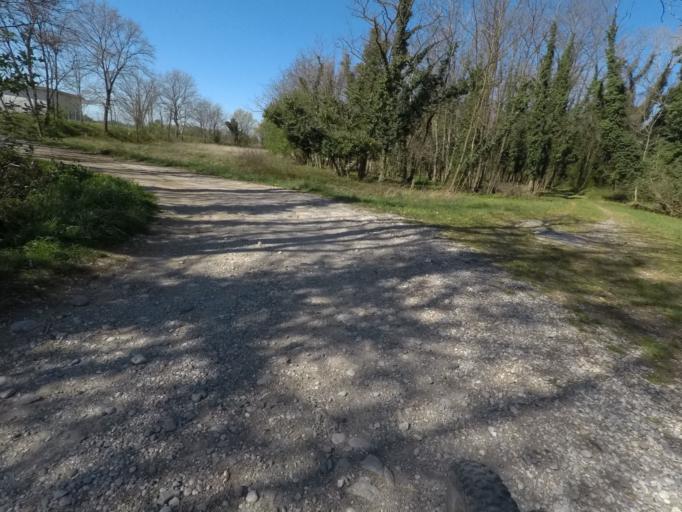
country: IT
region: Friuli Venezia Giulia
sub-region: Provincia di Udine
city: Moimacco
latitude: 46.0944
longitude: 13.3658
